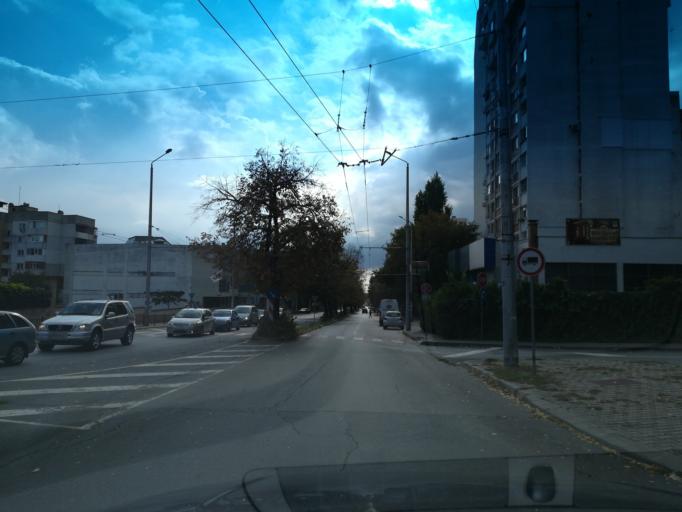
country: BG
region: Stara Zagora
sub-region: Obshtina Stara Zagora
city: Stara Zagora
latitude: 42.4368
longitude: 25.6310
